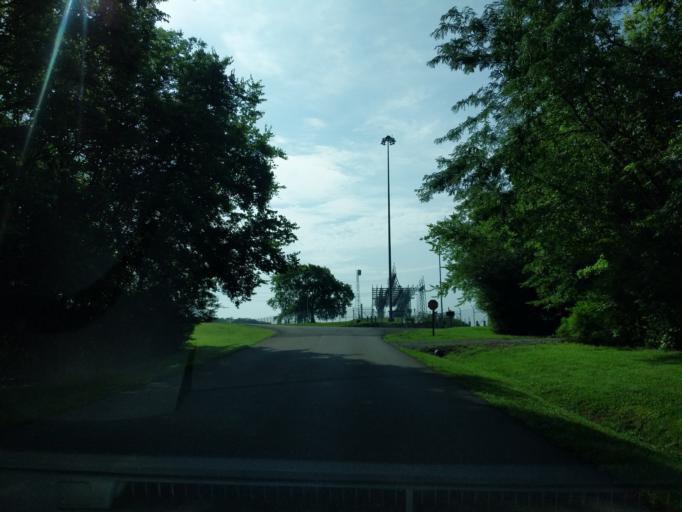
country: US
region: Tennessee
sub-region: Sumner County
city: Hendersonville
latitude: 36.2991
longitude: -86.6574
